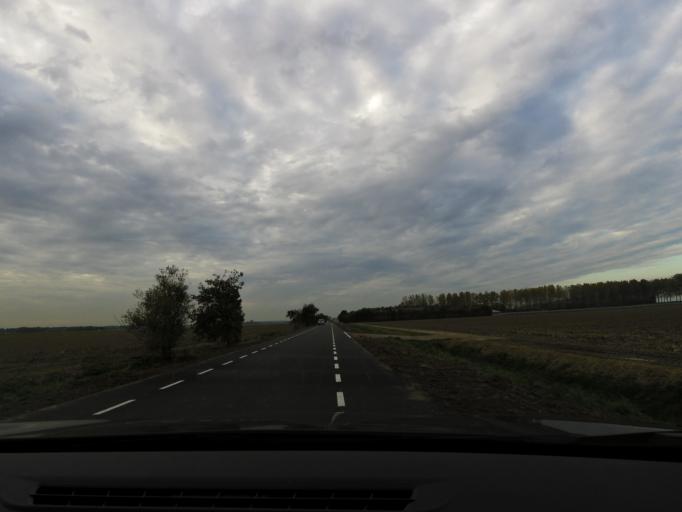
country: NL
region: South Holland
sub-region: Gemeente Goeree-Overflakkee
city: Dirksland
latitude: 51.7860
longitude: 4.0620
